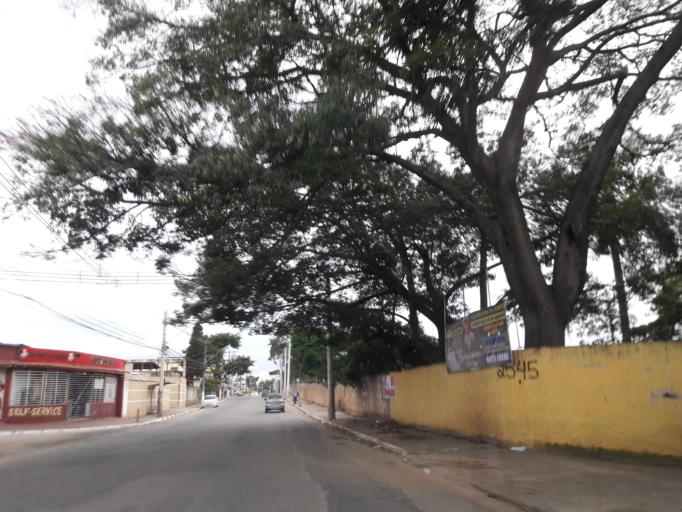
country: BR
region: Sao Paulo
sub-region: Aruja
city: Aruja
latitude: -23.4037
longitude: -46.4065
